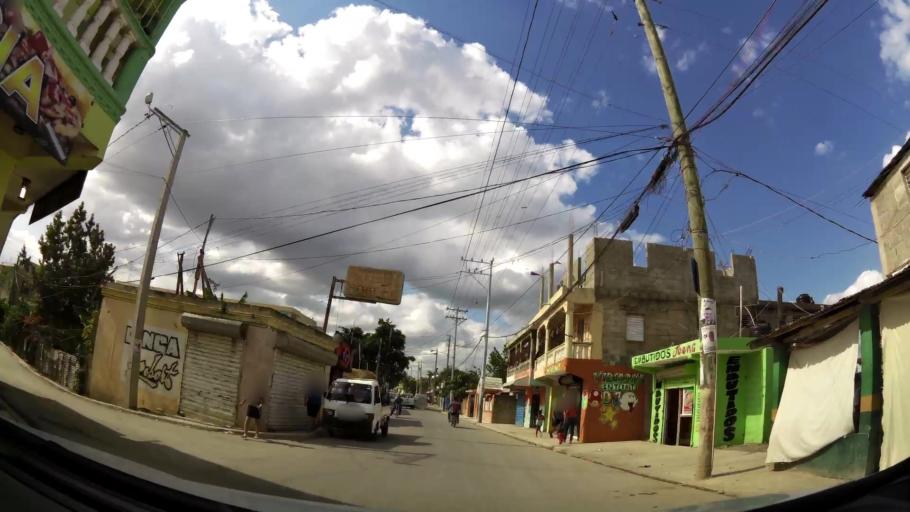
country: DO
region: Nacional
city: Ensanche Luperon
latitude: 18.5396
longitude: -69.8845
